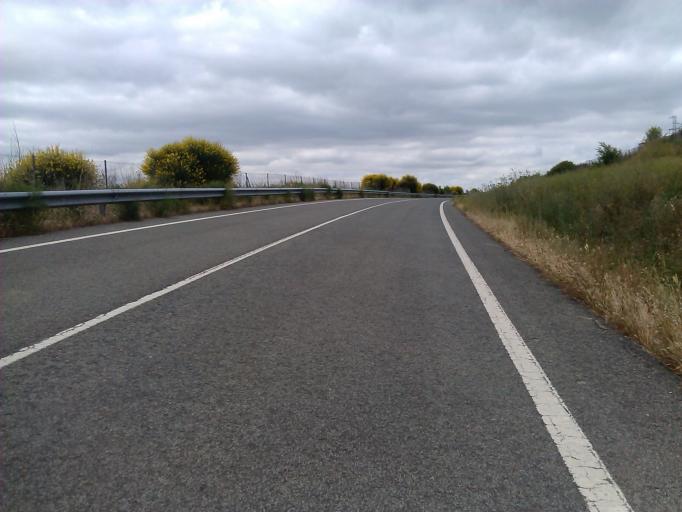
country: ES
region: Navarre
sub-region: Provincia de Navarra
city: Puente la Reina
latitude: 42.6684
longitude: -1.8316
